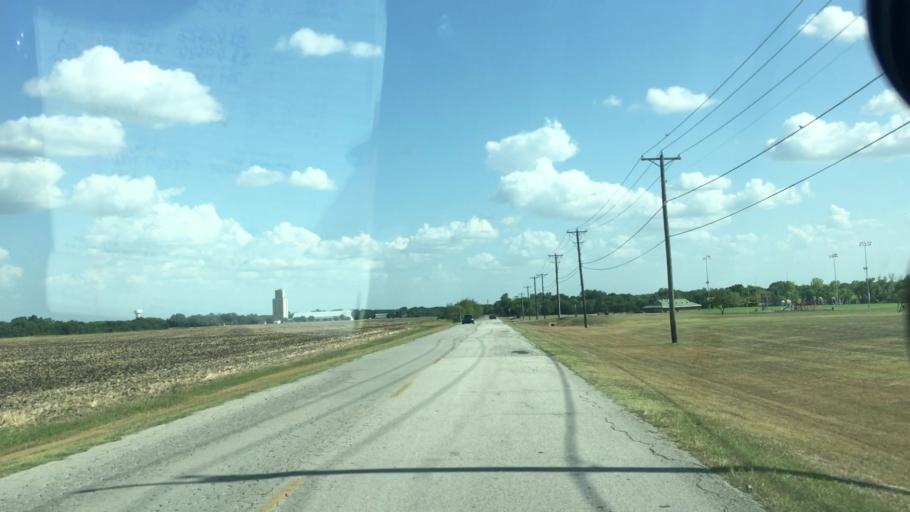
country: US
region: Texas
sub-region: Dallas County
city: Lancaster
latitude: 32.6139
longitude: -96.7526
